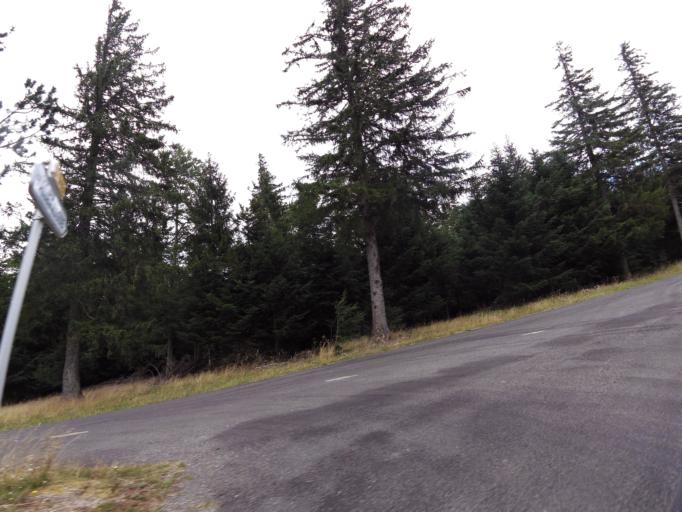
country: FR
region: Languedoc-Roussillon
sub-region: Departement du Gard
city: Valleraugue
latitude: 44.0897
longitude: 3.5557
